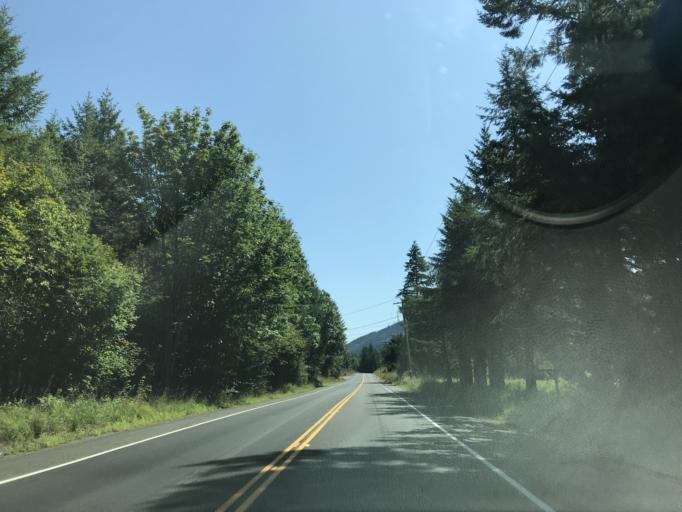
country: US
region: Washington
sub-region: King County
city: Ravensdale
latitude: 47.3579
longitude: -121.9119
